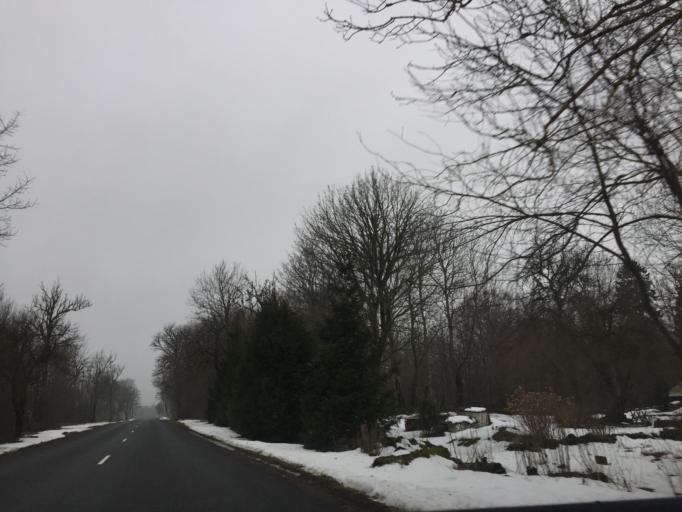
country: EE
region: Saare
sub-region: Orissaare vald
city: Orissaare
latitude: 58.3922
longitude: 22.8464
